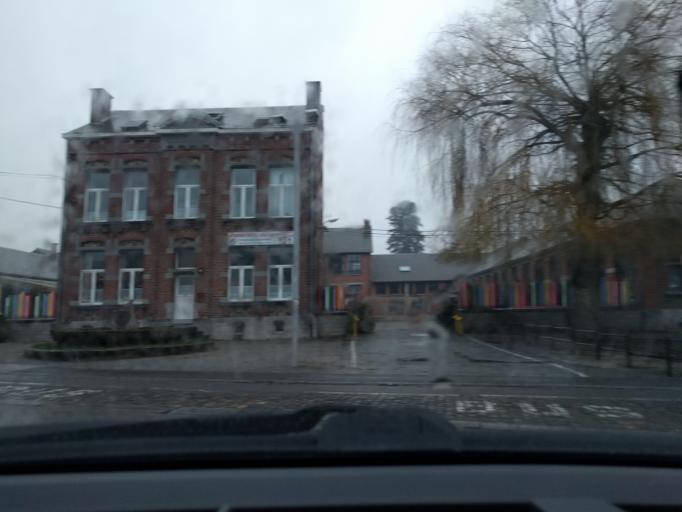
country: BE
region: Wallonia
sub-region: Province de Namur
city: Couvin
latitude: 50.0533
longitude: 4.4911
